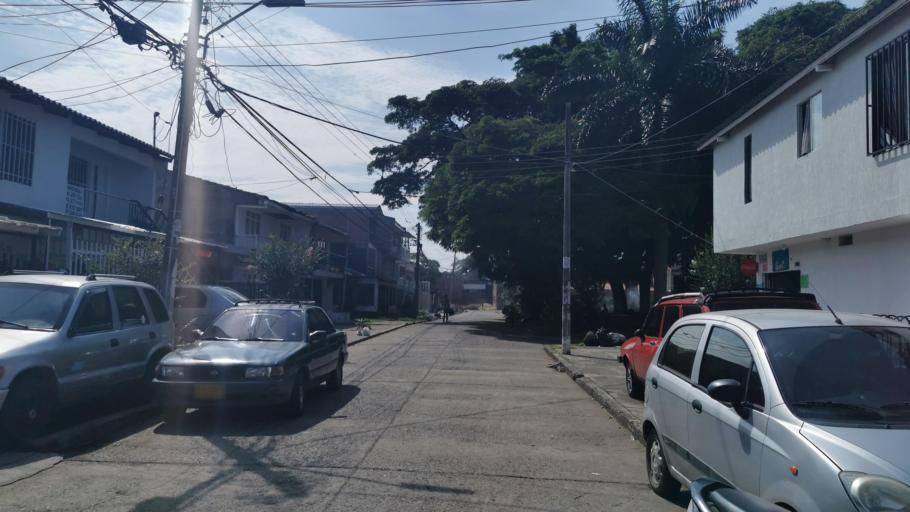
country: CO
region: Valle del Cauca
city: Jamundi
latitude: 3.2656
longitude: -76.5344
